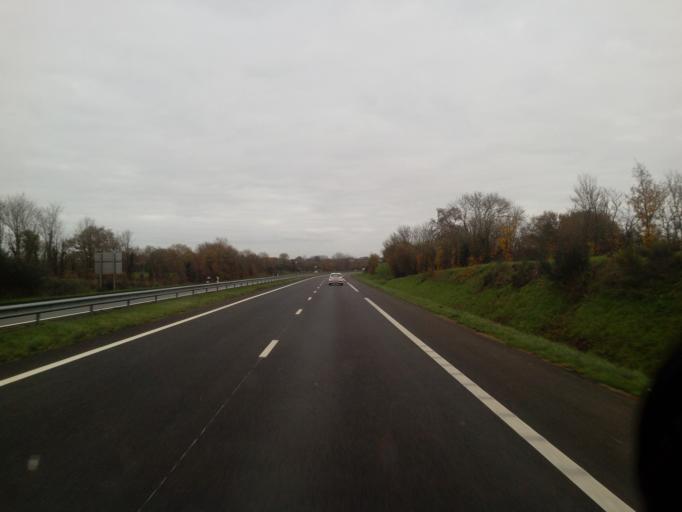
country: FR
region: Pays de la Loire
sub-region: Departement de Maine-et-Loire
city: Saint-Andre-de-la-Marche
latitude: 47.0896
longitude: -0.9899
